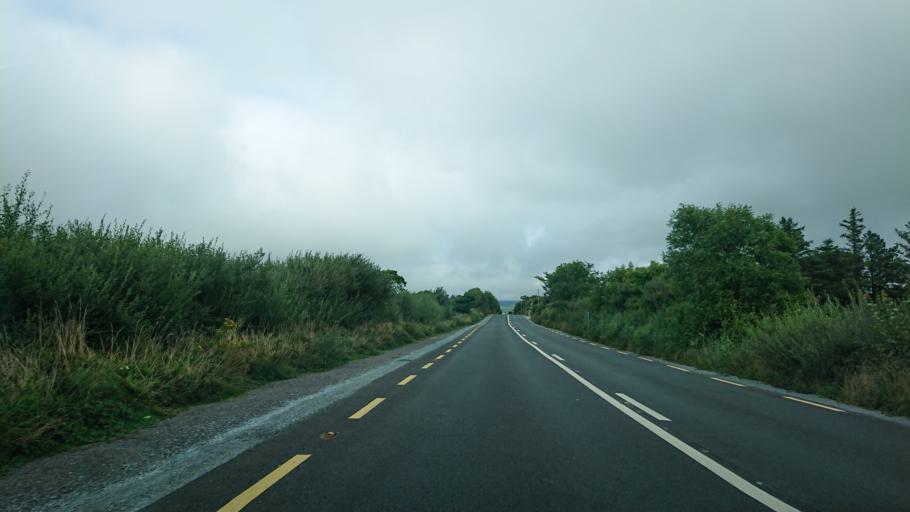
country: IE
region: Munster
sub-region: Ciarrai
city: Cahersiveen
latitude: 51.9638
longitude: -10.1771
